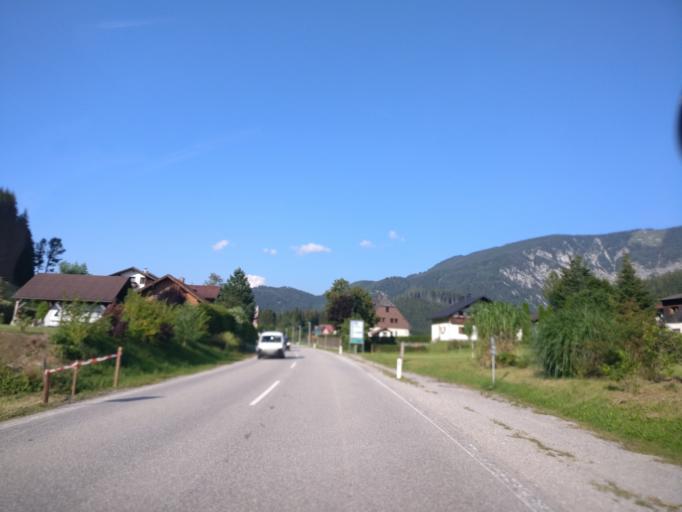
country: AT
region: Lower Austria
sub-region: Politischer Bezirk Scheibbs
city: Gostling an der Ybbs
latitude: 47.7446
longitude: 14.8945
